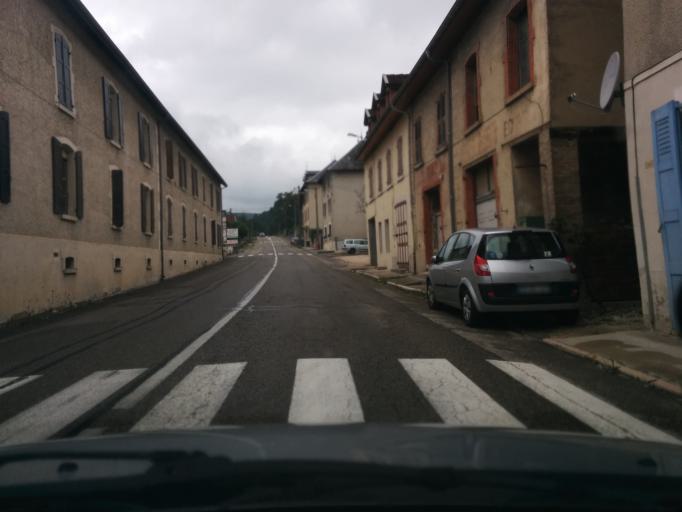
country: FR
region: Rhone-Alpes
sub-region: Departement de l'Isere
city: Saint-Geoire-en-Valdaine
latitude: 45.4659
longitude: 5.6519
